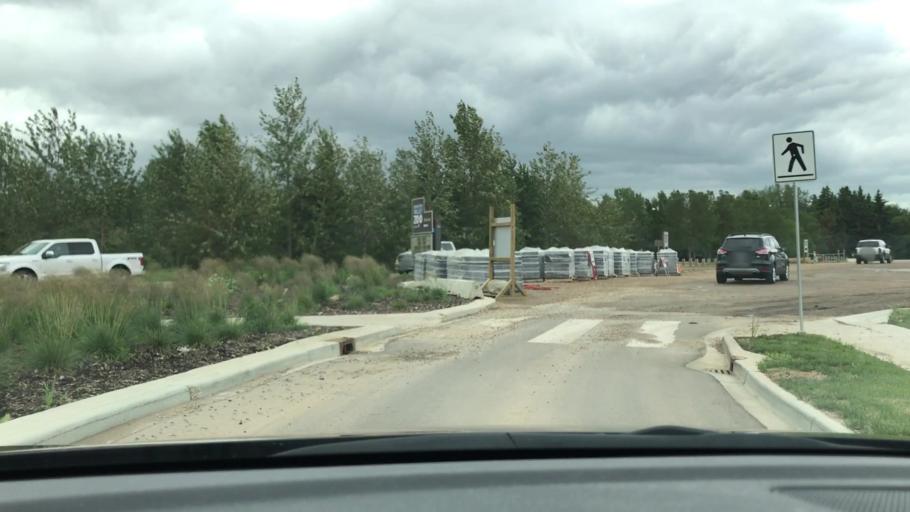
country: CA
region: Alberta
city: Edmonton
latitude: 53.5120
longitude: -113.5499
